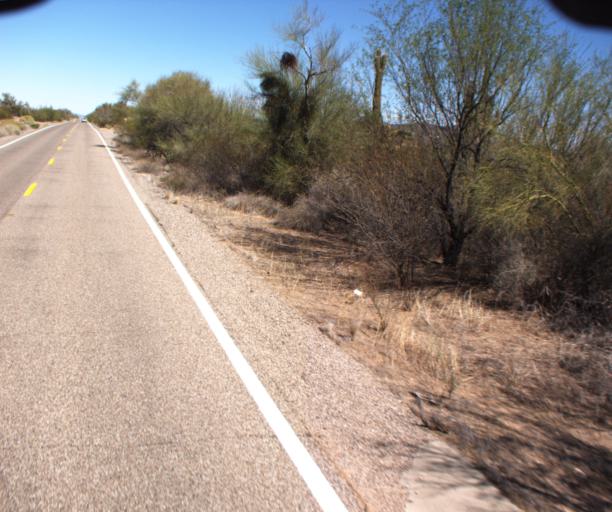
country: US
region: Arizona
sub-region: Pima County
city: Ajo
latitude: 32.1610
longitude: -112.7640
